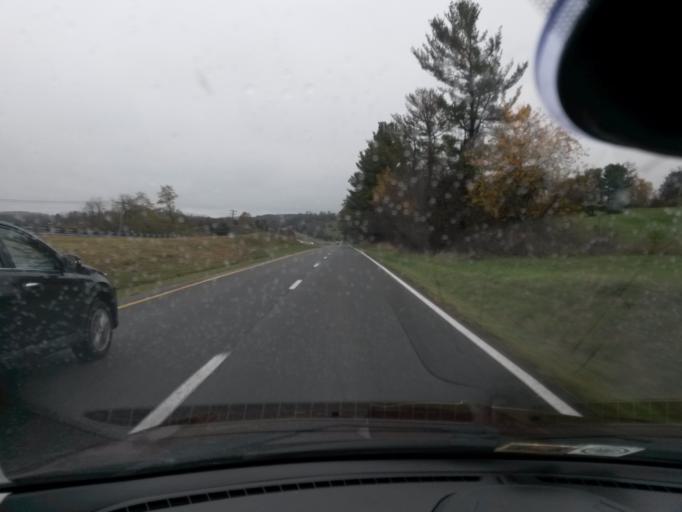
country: US
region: Virginia
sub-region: Botetourt County
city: Daleville
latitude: 37.4326
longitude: -79.9036
